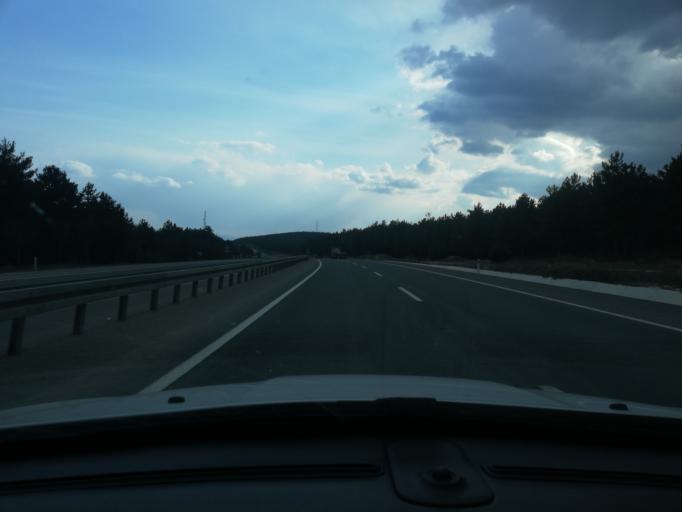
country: TR
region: Kastamonu
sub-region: Cide
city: Kastamonu
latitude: 41.3921
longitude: 33.7499
